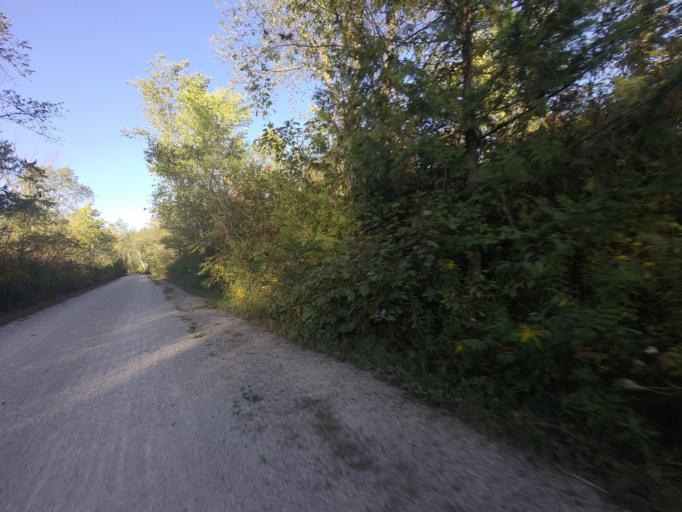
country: CA
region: Ontario
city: Brampton
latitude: 43.8259
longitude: -79.9124
